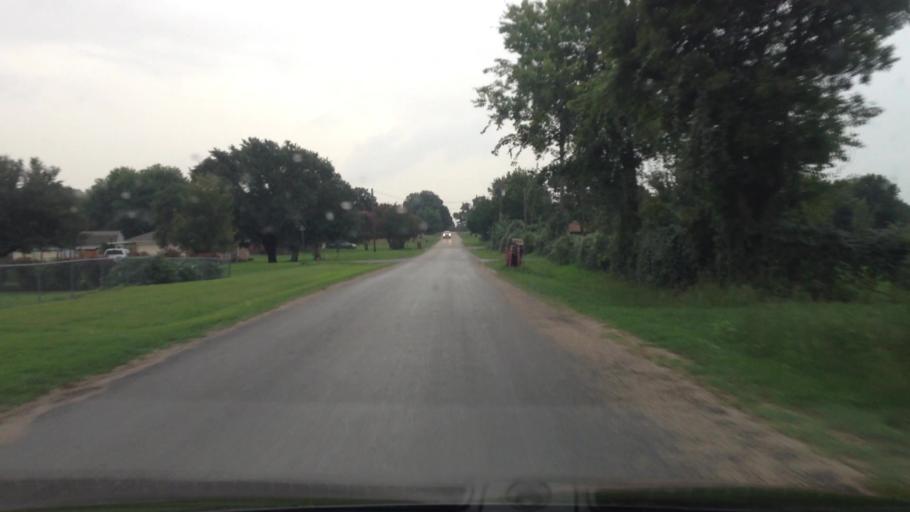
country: US
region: Texas
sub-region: Johnson County
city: Joshua
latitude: 32.4822
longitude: -97.3437
